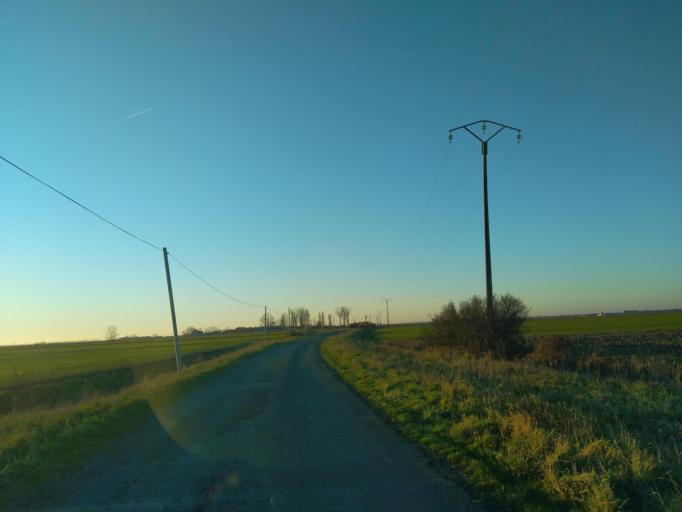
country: FR
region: Pays de la Loire
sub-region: Departement de la Vendee
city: Triaize
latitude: 46.3712
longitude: -1.2726
